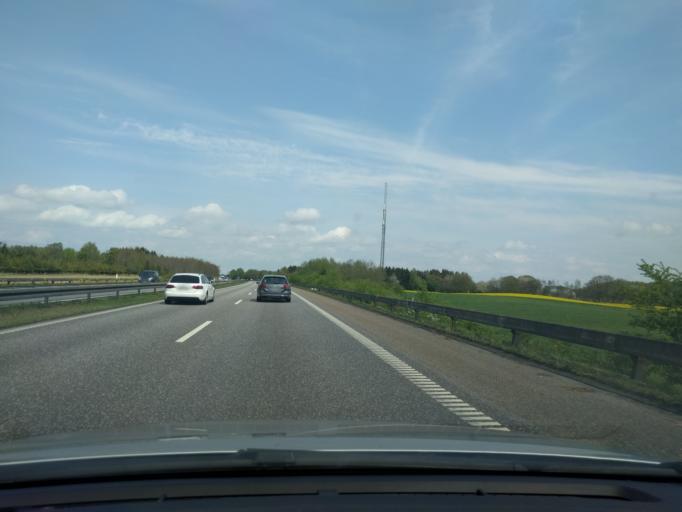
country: DK
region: Zealand
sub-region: Soro Kommune
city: Soro
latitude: 55.4424
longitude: 11.5102
